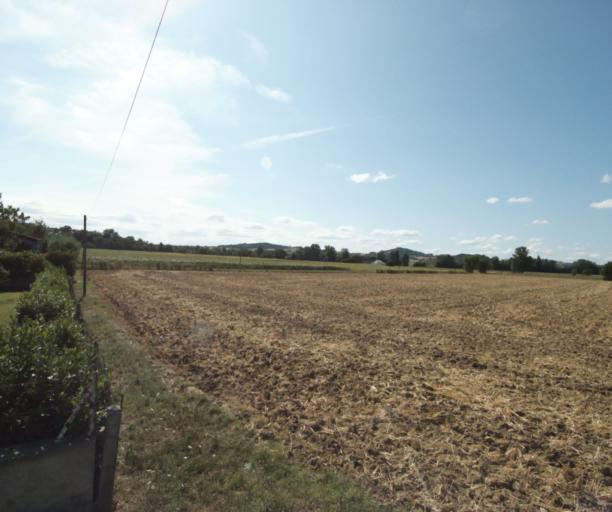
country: FR
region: Midi-Pyrenees
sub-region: Departement de la Haute-Garonne
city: Revel
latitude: 43.5003
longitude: 1.9719
